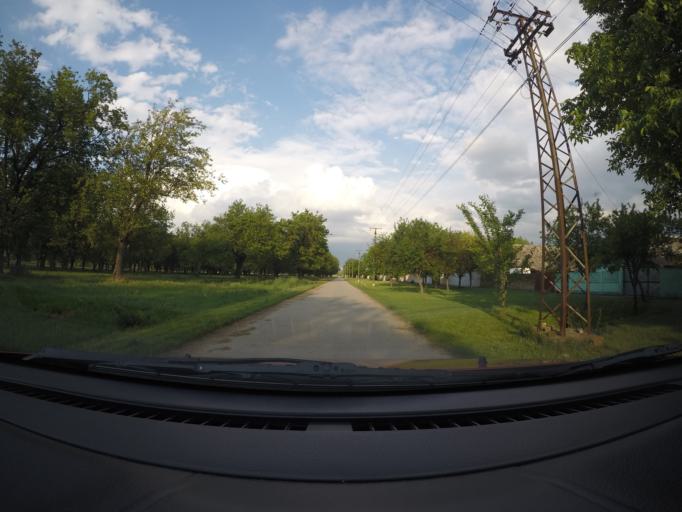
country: RS
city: Debeljaca
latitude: 45.0634
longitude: 20.6037
